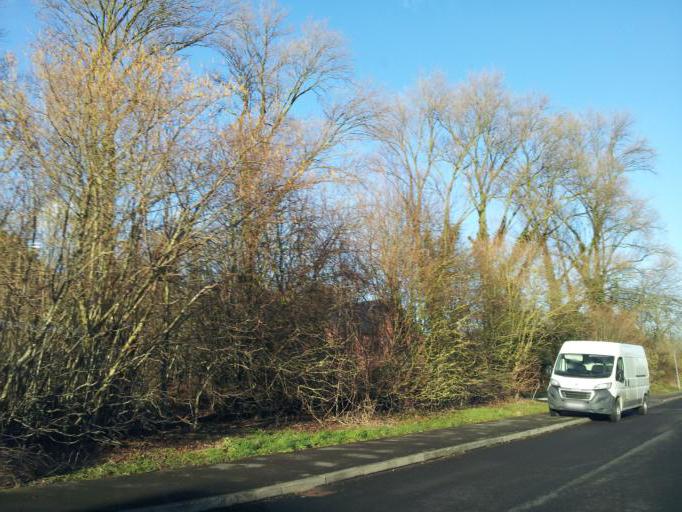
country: GB
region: England
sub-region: Nottinghamshire
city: Newark on Trent
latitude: 53.0757
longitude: -0.7748
